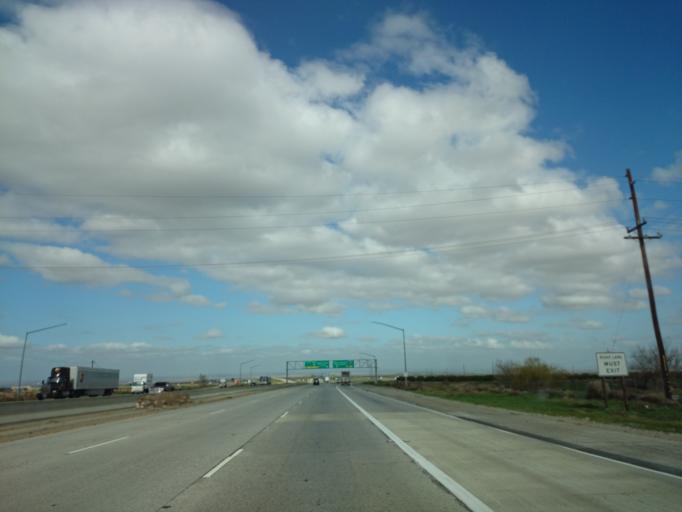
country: US
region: California
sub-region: Kern County
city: Frazier Park
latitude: 35.0051
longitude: -118.9511
